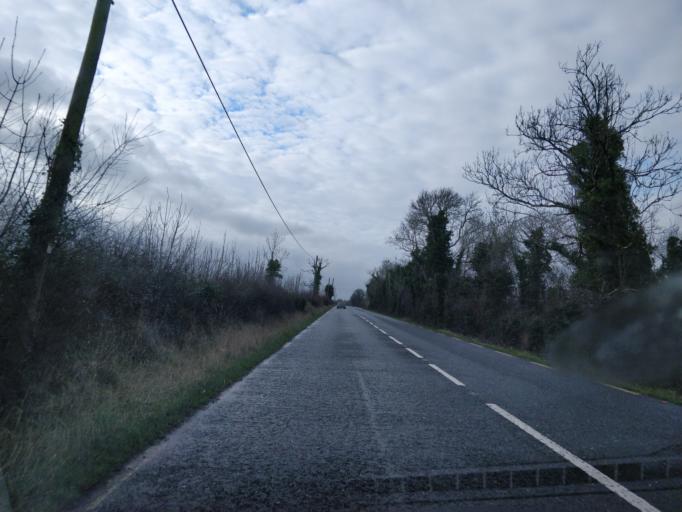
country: IE
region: Connaught
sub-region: Roscommon
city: Roscommon
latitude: 53.7688
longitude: -8.1585
